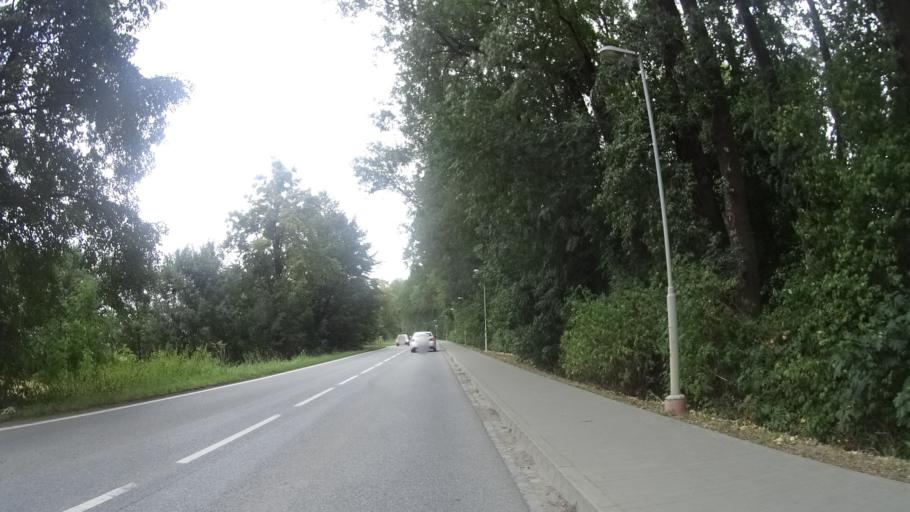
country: CZ
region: Olomoucky
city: Tovacov
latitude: 49.4220
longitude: 17.2906
